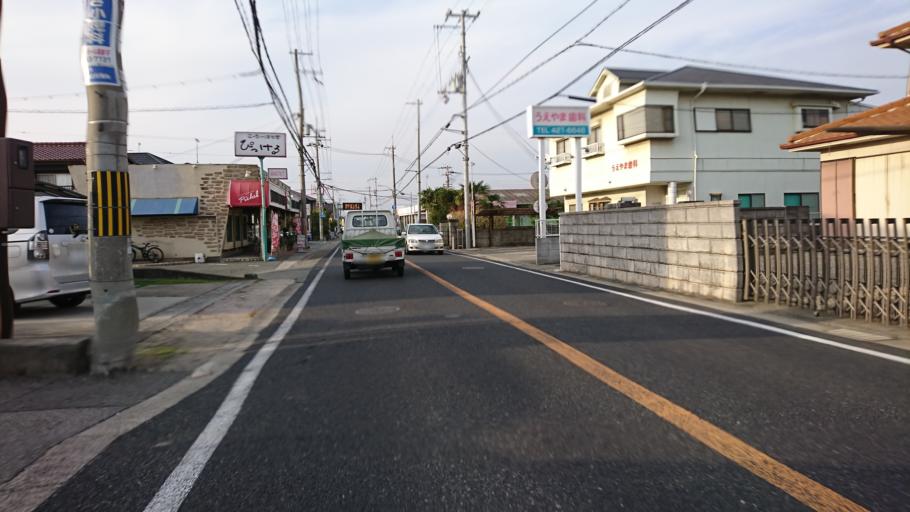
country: JP
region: Hyogo
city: Kakogawacho-honmachi
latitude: 34.7446
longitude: 134.8200
